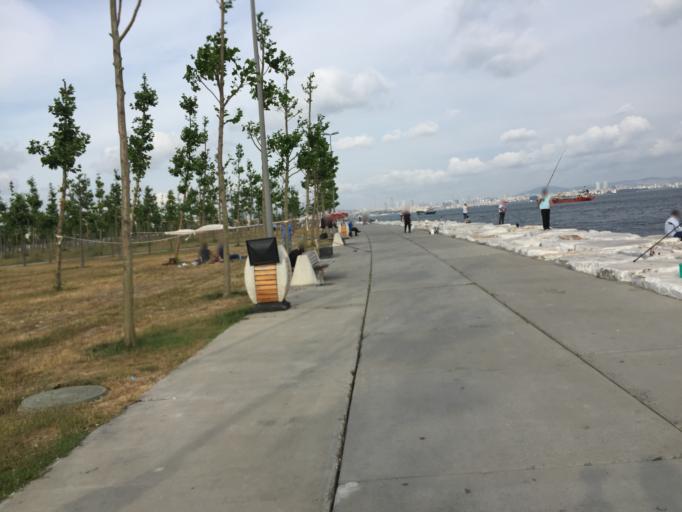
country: TR
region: Istanbul
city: Istanbul
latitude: 40.9964
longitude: 28.9474
